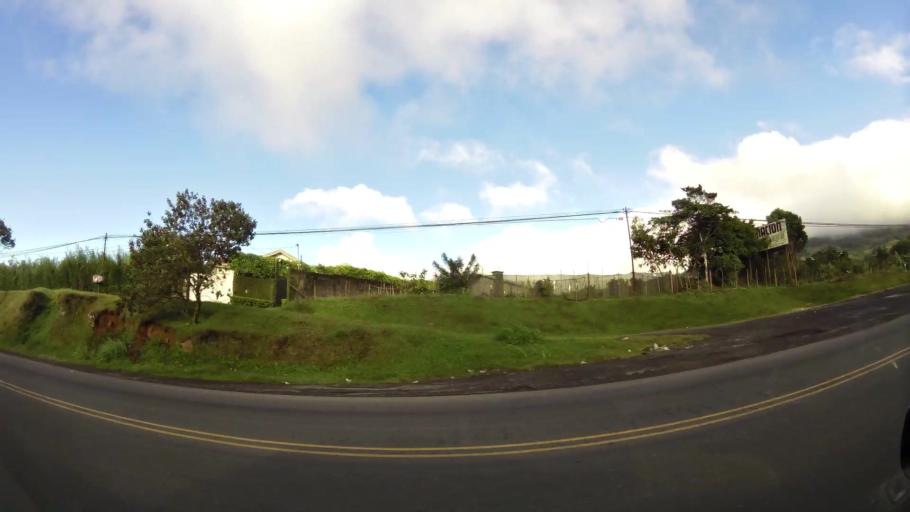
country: CR
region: Heredia
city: Angeles
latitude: 10.0258
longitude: -84.0247
